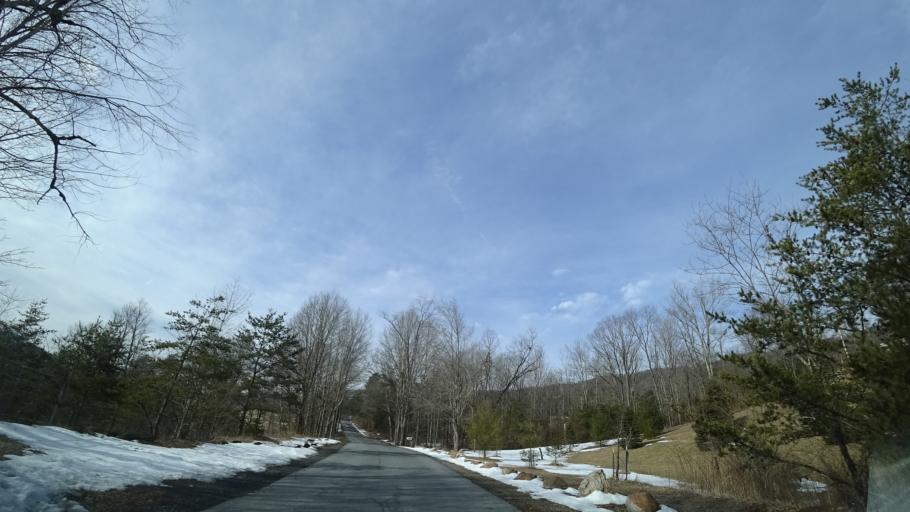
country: US
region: Virginia
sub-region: Shenandoah County
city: Edinburg
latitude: 38.9802
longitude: -78.6671
